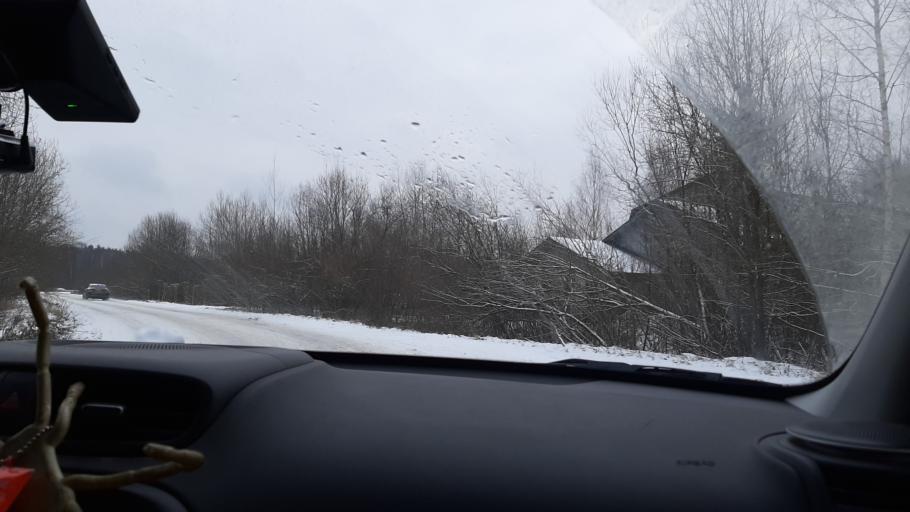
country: RU
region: Ivanovo
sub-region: Gorod Ivanovo
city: Ivanovo
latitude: 56.9288
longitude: 40.9771
